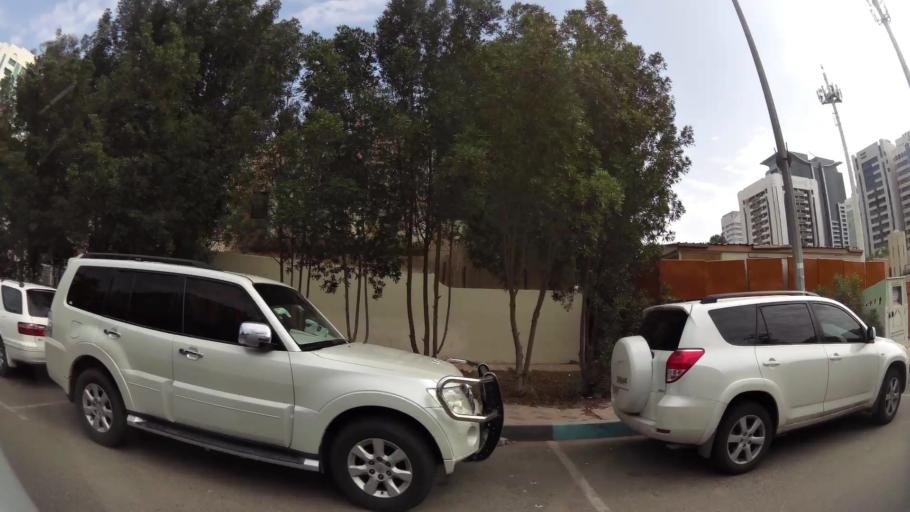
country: AE
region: Abu Dhabi
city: Abu Dhabi
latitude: 24.4800
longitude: 54.3529
